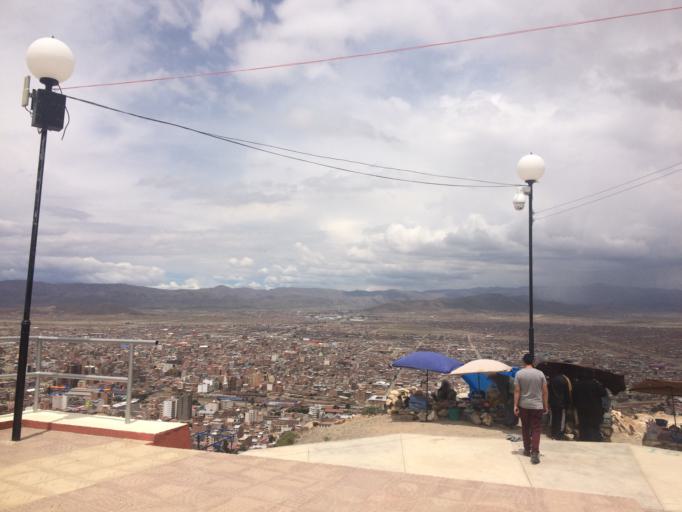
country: BO
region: Oruro
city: Oruro
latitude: -17.9748
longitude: -67.1199
